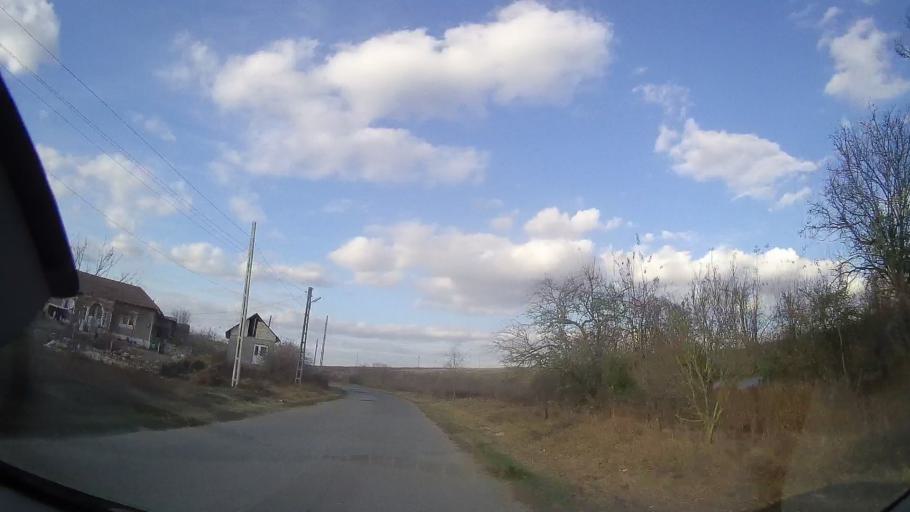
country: RO
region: Constanta
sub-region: Comuna Cerchezu
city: Cerchezu
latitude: 43.8266
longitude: 28.0978
